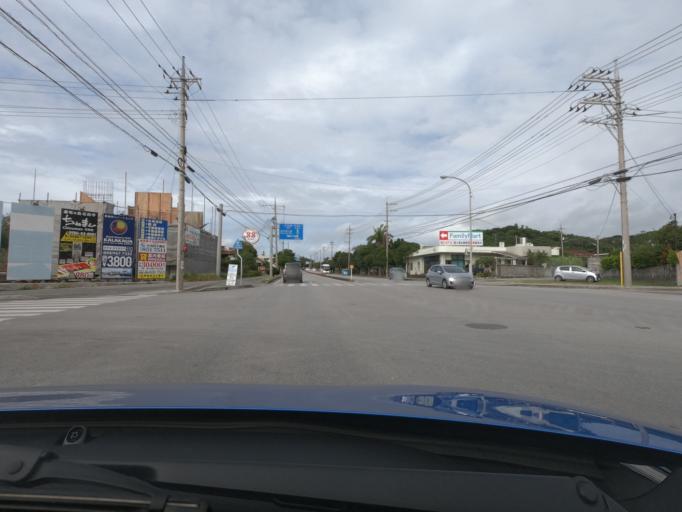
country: JP
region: Okinawa
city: Nago
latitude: 26.6752
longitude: 127.8910
